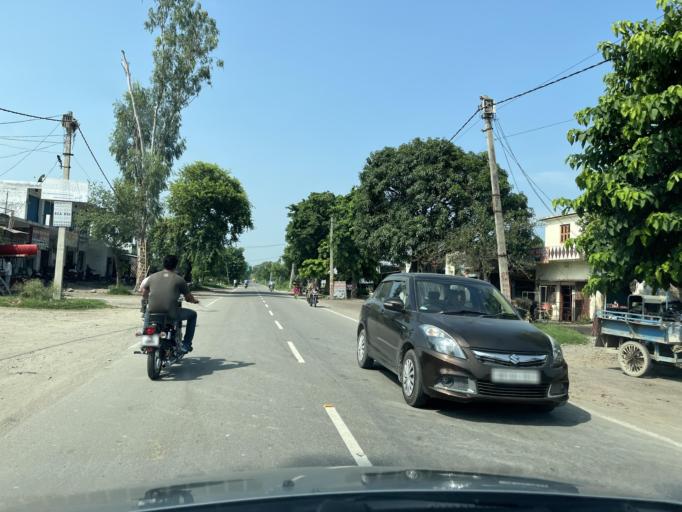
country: IN
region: Uttarakhand
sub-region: Udham Singh Nagar
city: Bazpur
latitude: 29.2045
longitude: 79.2085
